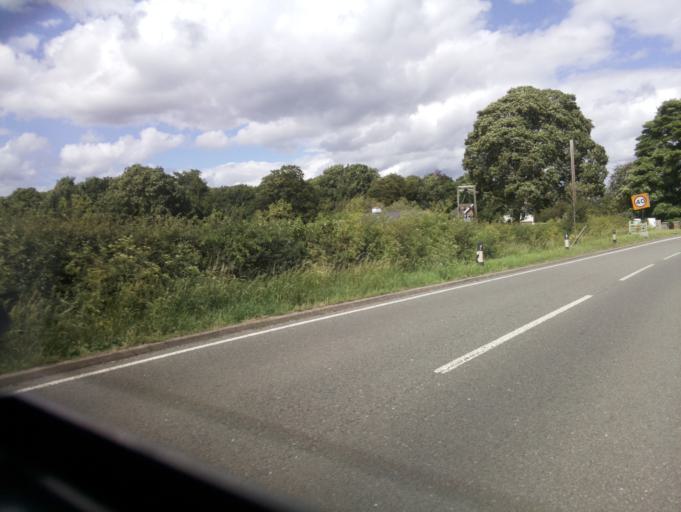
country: GB
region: England
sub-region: Nottinghamshire
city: Cotgrave
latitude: 52.9011
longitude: -1.0778
